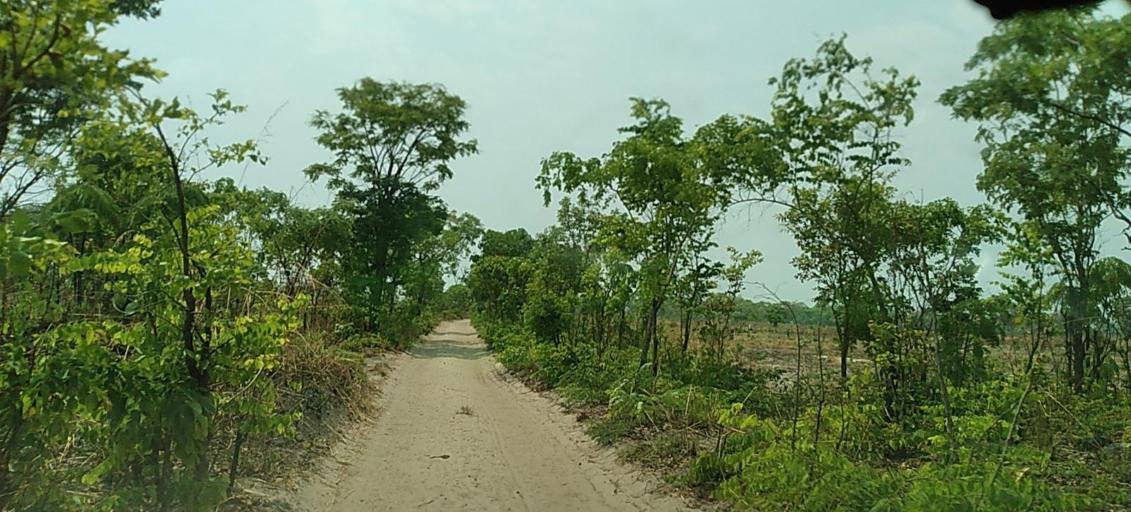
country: ZM
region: North-Western
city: Kabompo
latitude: -13.4680
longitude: 24.4412
